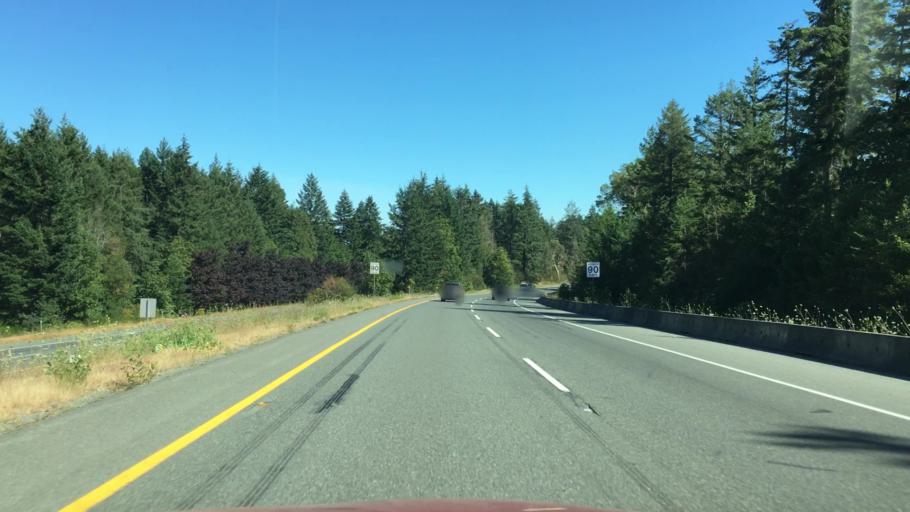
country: CA
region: British Columbia
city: Nanaimo
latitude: 49.1400
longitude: -123.9603
